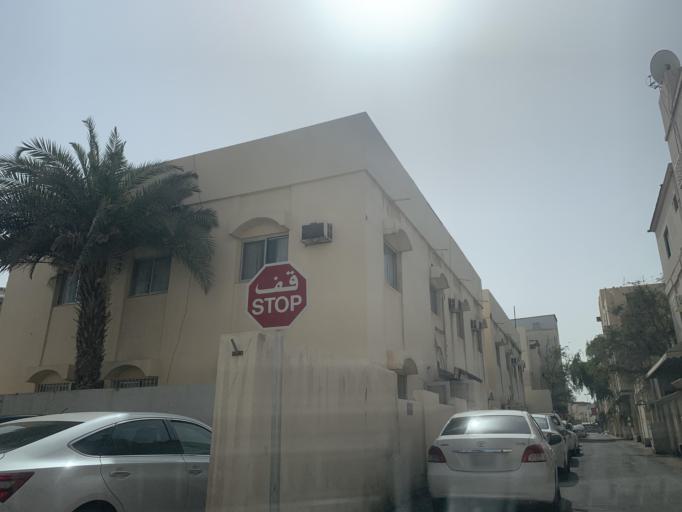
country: BH
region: Northern
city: Madinat `Isa
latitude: 26.1829
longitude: 50.5471
